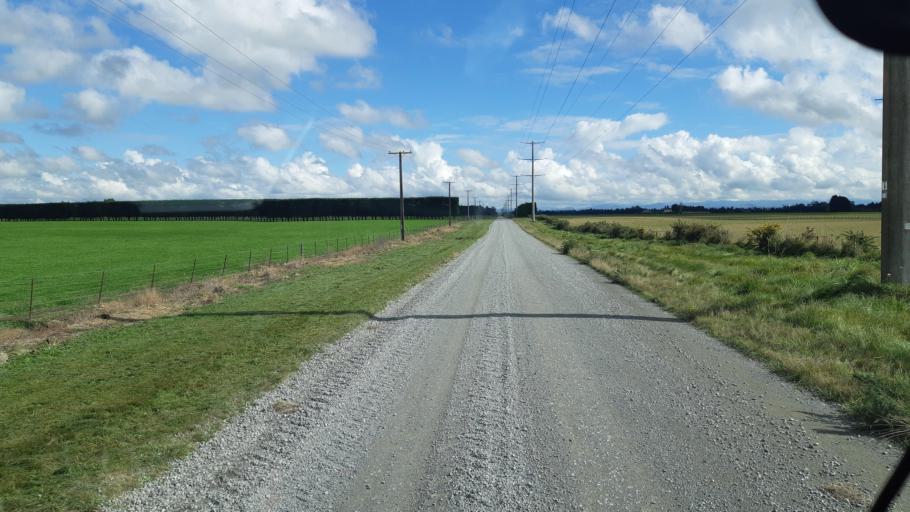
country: NZ
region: Canterbury
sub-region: Selwyn District
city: Darfield
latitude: -43.4728
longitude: 172.2555
